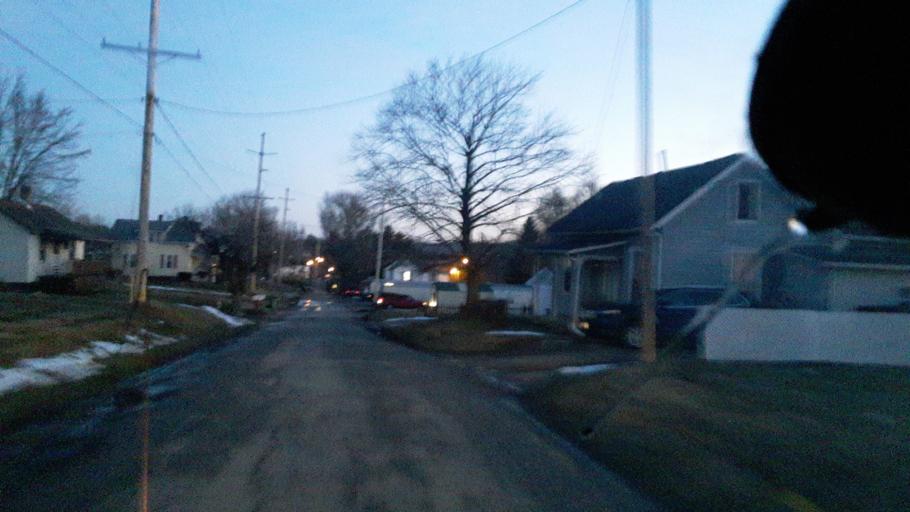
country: US
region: Ohio
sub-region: Perry County
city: New Lexington
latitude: 39.7093
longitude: -82.2159
